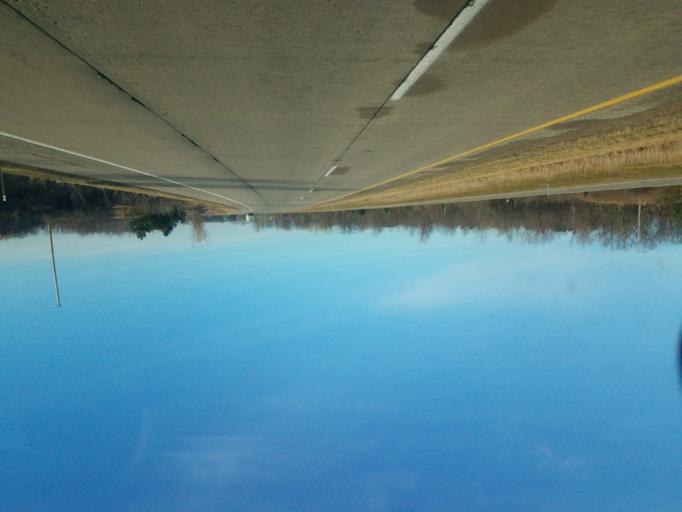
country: US
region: Michigan
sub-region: Clinton County
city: DeWitt
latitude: 42.8262
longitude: -84.5179
